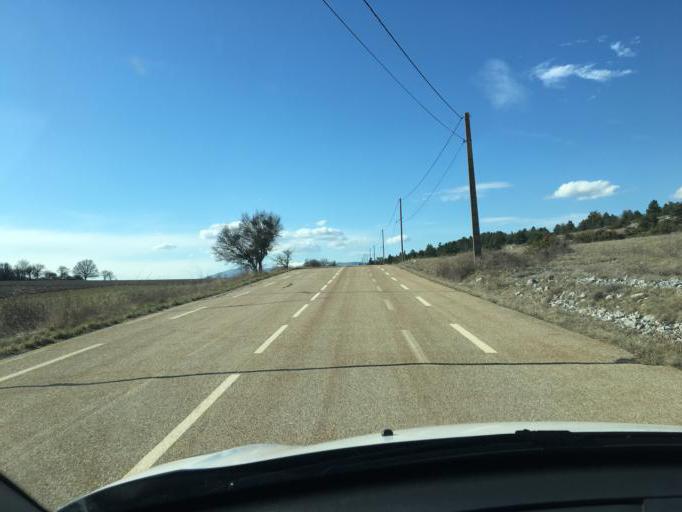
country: FR
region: Provence-Alpes-Cote d'Azur
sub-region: Departement du Vaucluse
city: Sault
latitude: 44.0353
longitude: 5.4542
